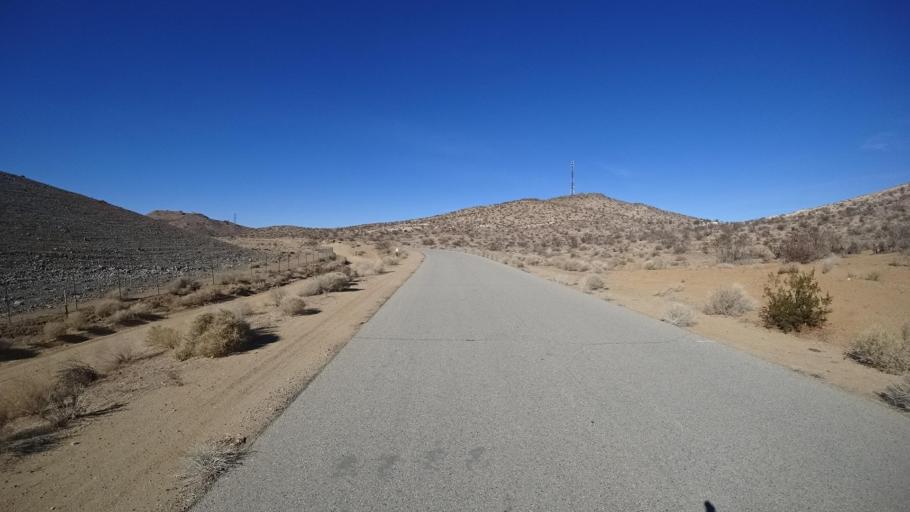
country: US
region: California
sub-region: Kern County
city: Ridgecrest
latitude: 35.3573
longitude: -117.6375
